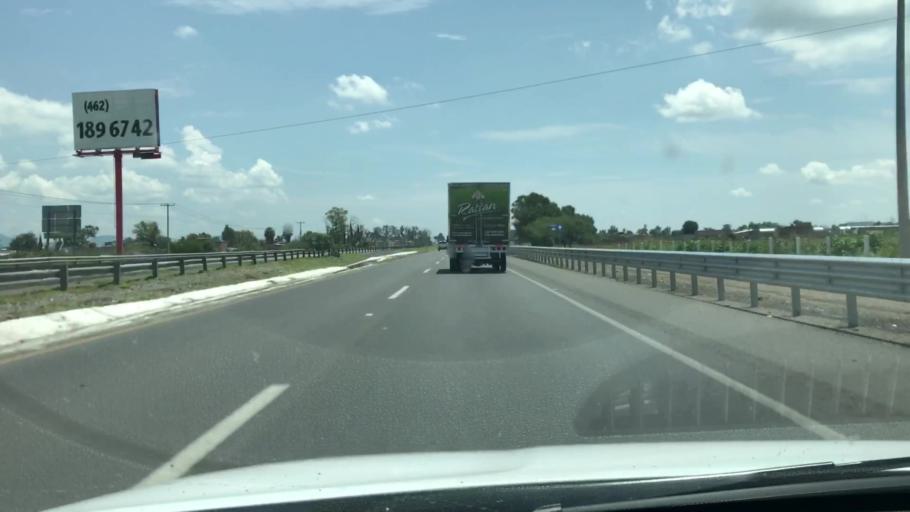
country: MX
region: Guanajuato
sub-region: Irapuato
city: Las Huertas Tercera Seccion
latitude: 20.6496
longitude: -101.3705
